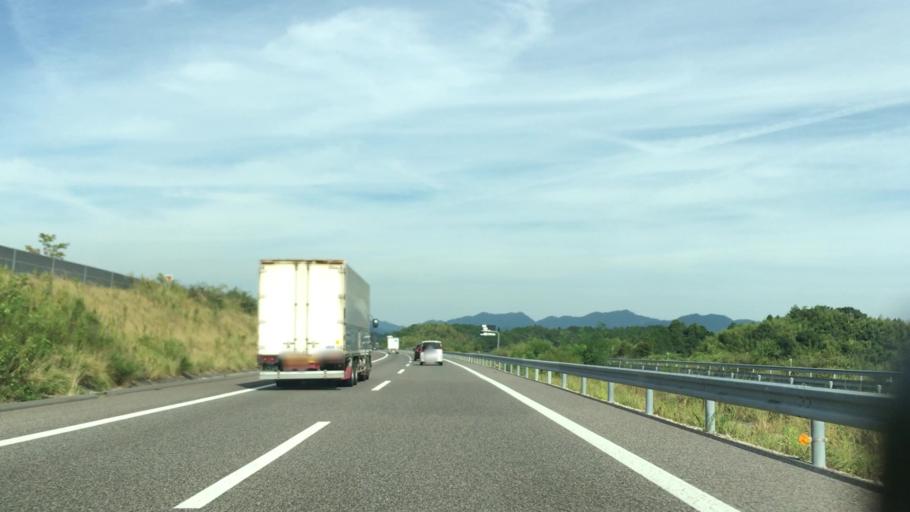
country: JP
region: Shiga Prefecture
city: Minakuchicho-matoba
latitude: 34.9102
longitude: 136.1696
